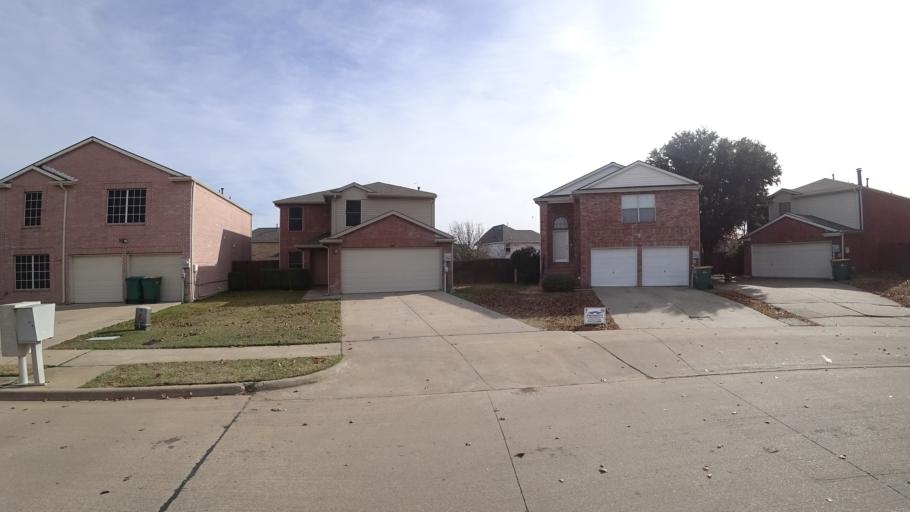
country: US
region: Texas
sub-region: Denton County
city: Highland Village
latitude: 33.0740
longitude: -97.0319
